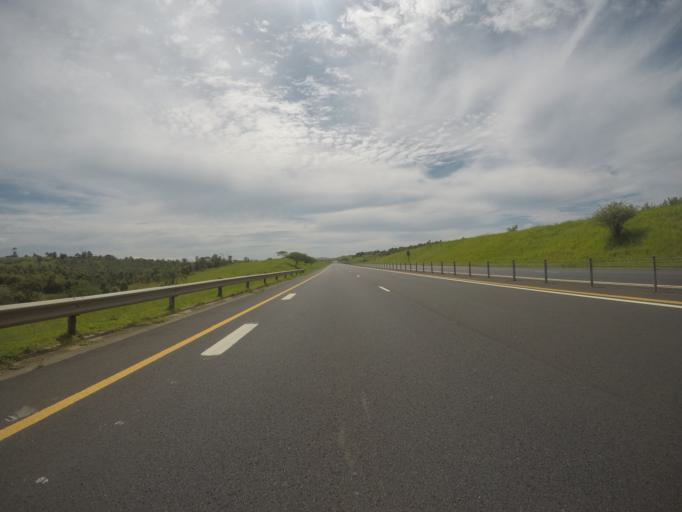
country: ZA
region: KwaZulu-Natal
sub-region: iLembe District Municipality
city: Mandeni
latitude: -29.1820
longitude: 31.4903
